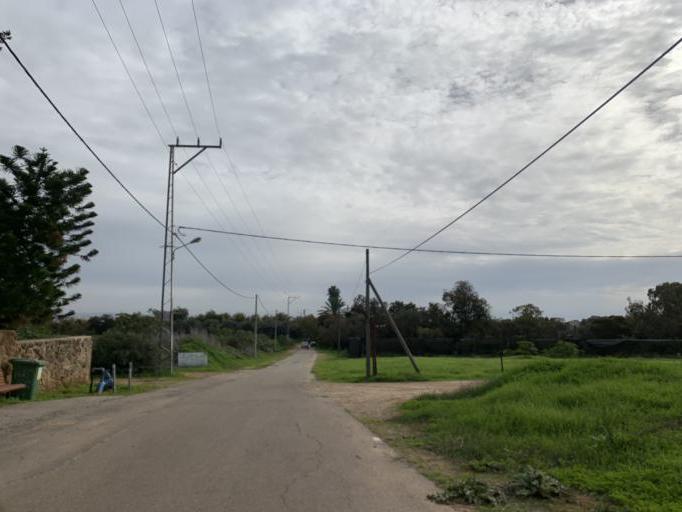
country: IL
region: Central District
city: Hod HaSharon
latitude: 32.1497
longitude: 34.9047
